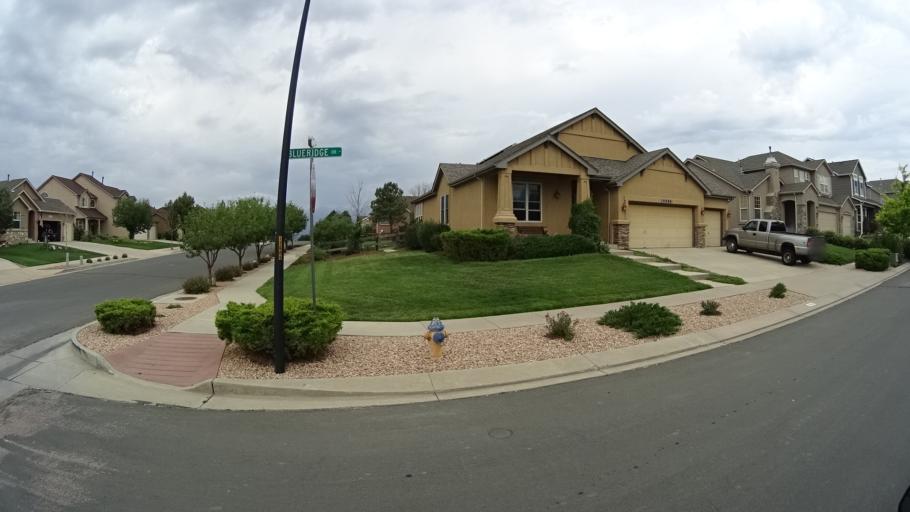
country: US
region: Colorado
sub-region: El Paso County
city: Gleneagle
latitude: 39.0026
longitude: -104.7910
